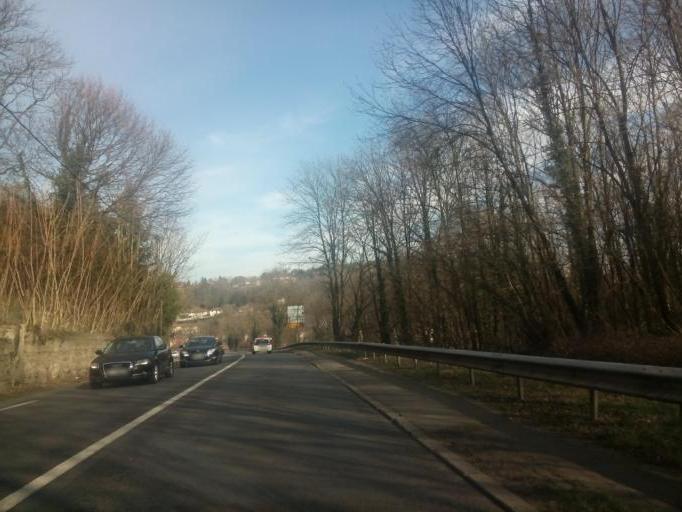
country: FR
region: Rhone-Alpes
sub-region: Departement du Rhone
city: Francheville
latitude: 45.7215
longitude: 4.7790
